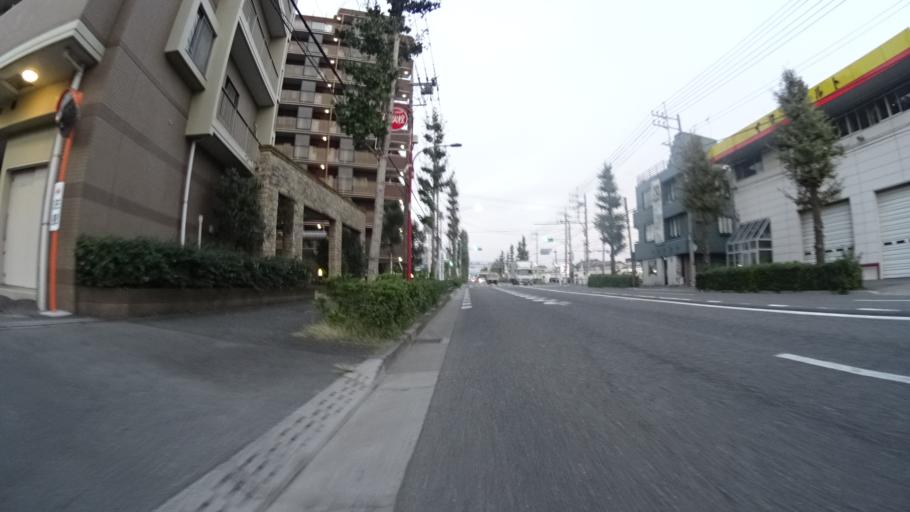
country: JP
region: Tokyo
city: Hino
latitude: 35.6950
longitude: 139.3830
